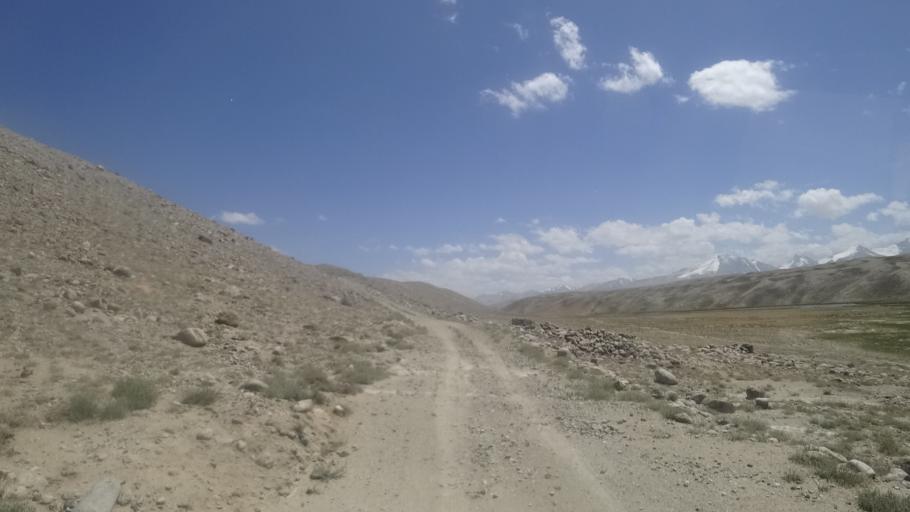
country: TJ
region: Gorno-Badakhshan
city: Murghob
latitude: 37.4645
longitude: 73.3496
